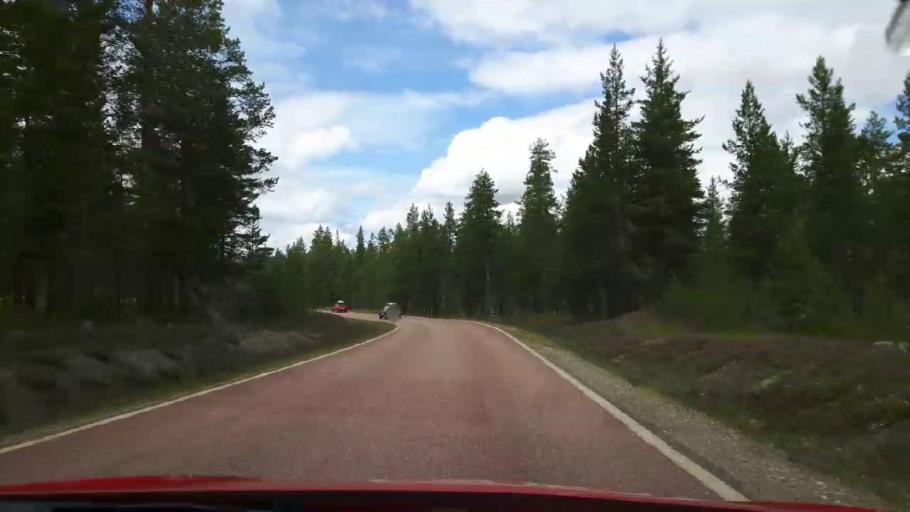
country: NO
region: Hedmark
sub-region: Trysil
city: Innbygda
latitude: 61.8499
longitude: 12.9538
